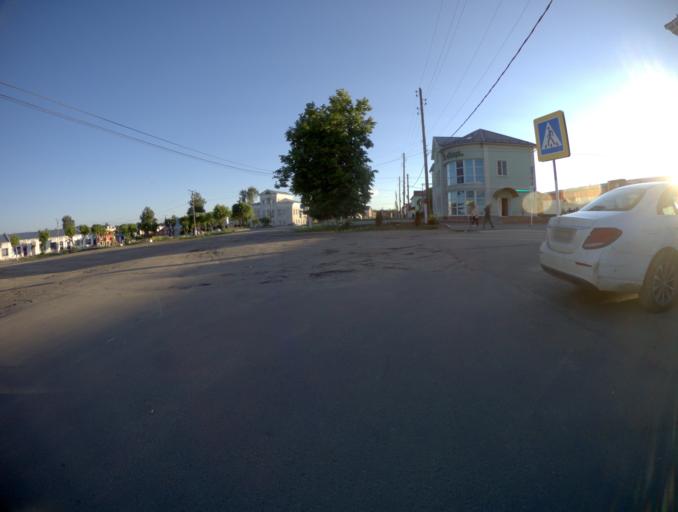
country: RU
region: Ivanovo
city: Gavrilov Posad
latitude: 56.5590
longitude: 40.1206
